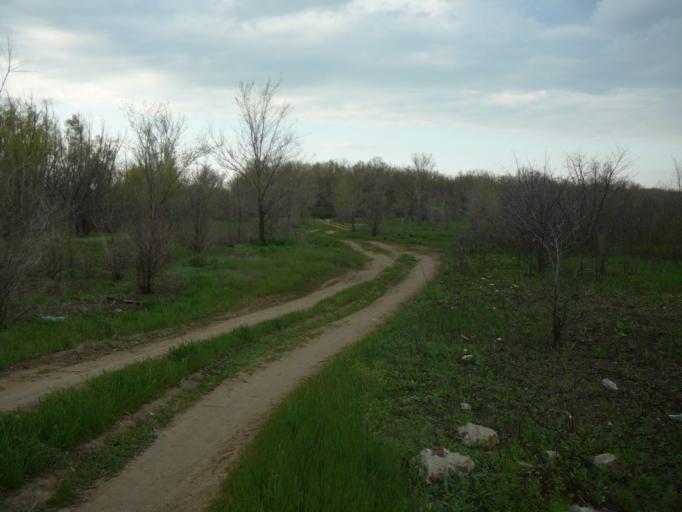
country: RU
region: Saratov
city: Engel's
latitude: 51.4581
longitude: 46.1729
